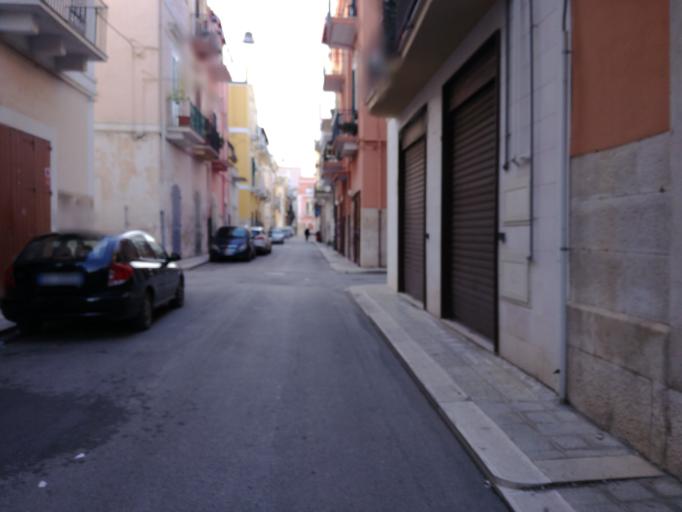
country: IT
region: Apulia
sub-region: Provincia di Bari
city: Corato
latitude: 41.1497
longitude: 16.4168
